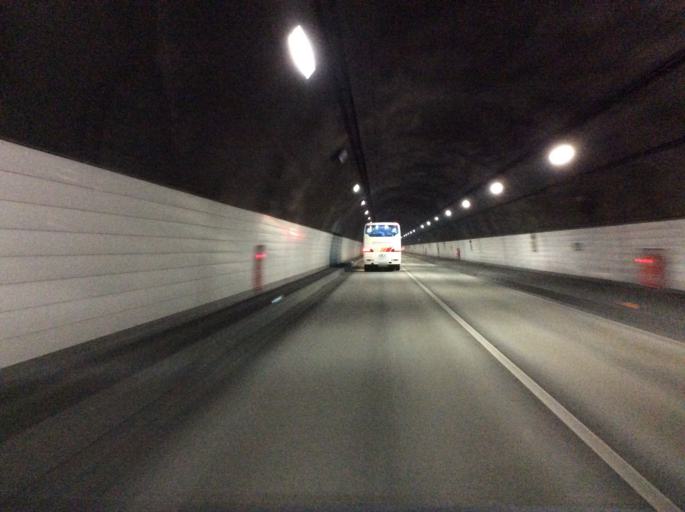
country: JP
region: Fukushima
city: Iwaki
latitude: 37.0962
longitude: 140.7795
